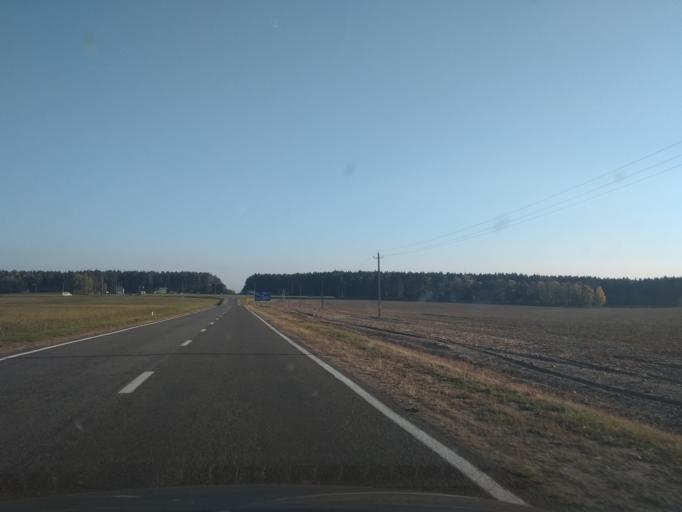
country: BY
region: Grodnenskaya
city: Vawkavysk
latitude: 53.1493
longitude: 24.5009
